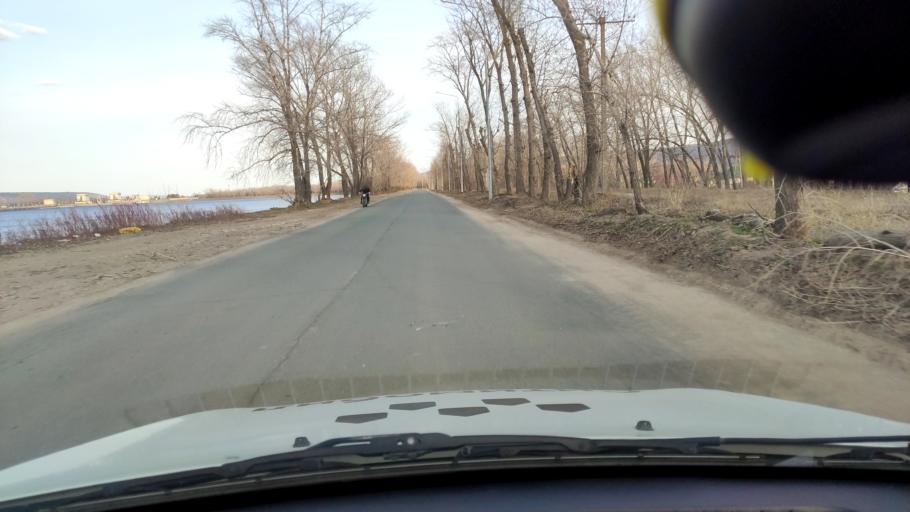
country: RU
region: Samara
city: Zhigulevsk
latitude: 53.4573
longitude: 49.5401
